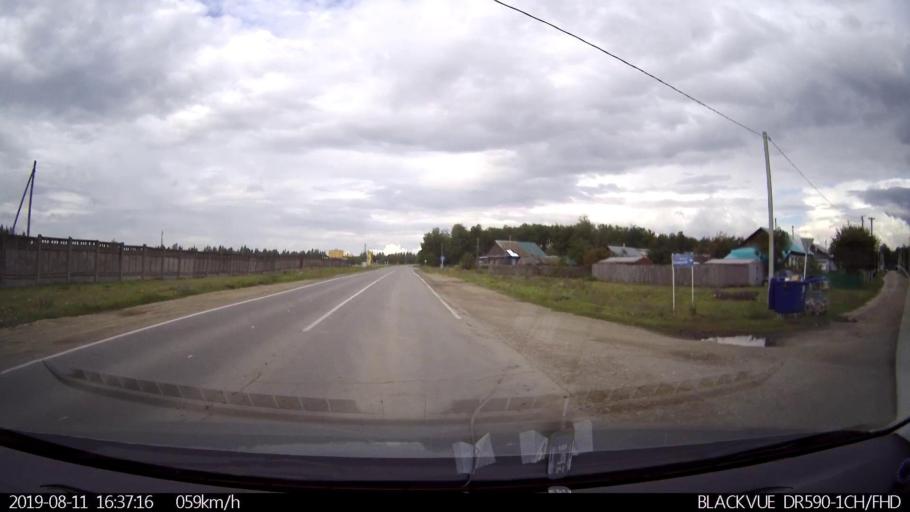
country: RU
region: Ulyanovsk
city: Mayna
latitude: 54.1260
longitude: 47.6134
